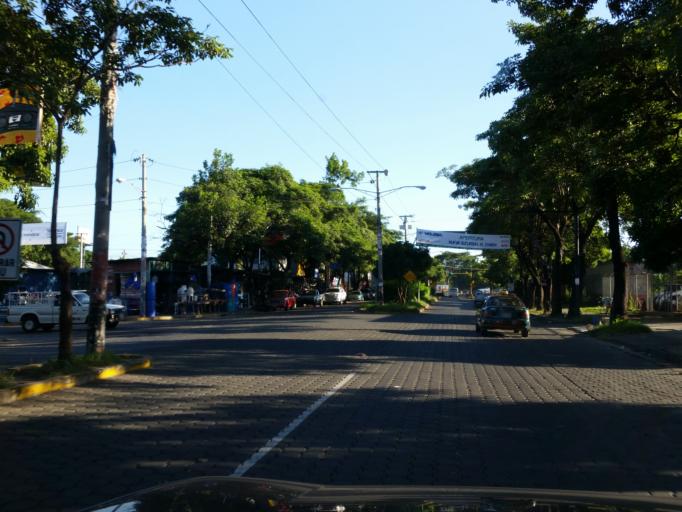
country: NI
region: Managua
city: Managua
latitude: 12.1267
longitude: -86.3013
